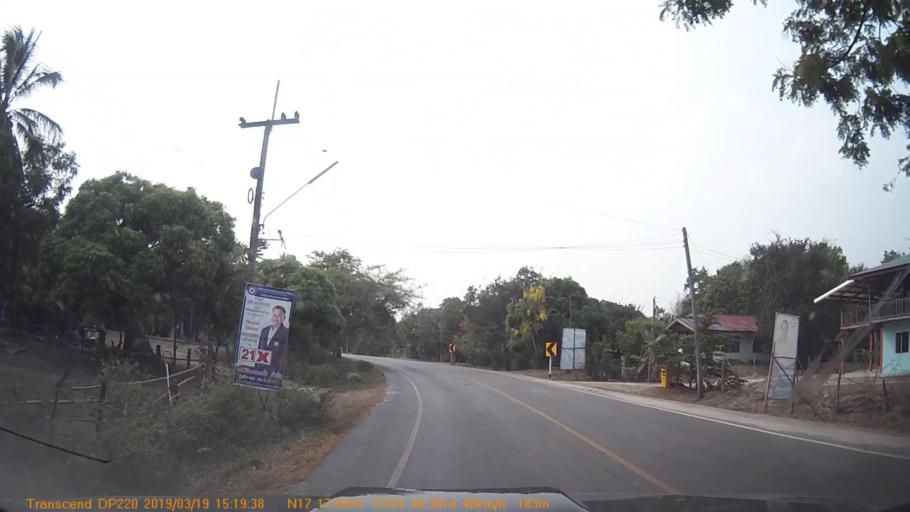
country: TH
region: Sakon Nakhon
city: Phanna Nikhom
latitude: 17.2936
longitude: 103.7715
